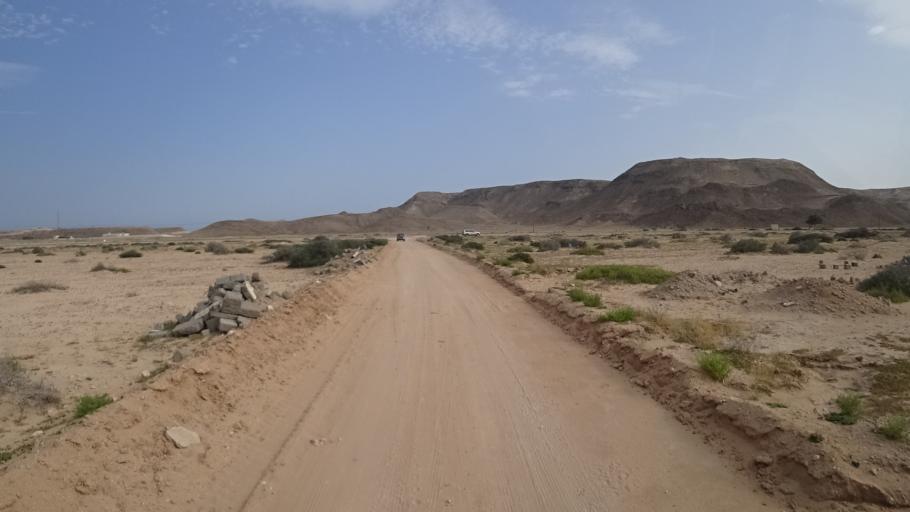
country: OM
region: Ash Sharqiyah
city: Sur
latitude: 22.4365
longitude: 59.8175
